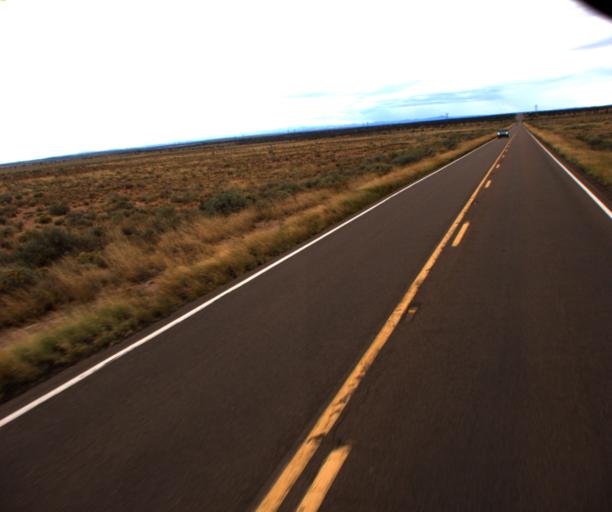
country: US
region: Arizona
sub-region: Navajo County
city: Snowflake
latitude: 34.6654
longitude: -110.1009
